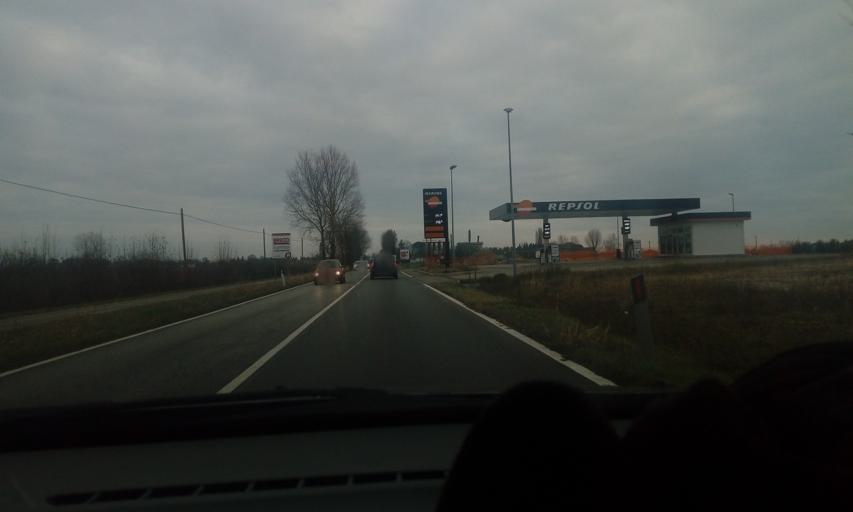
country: IT
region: Friuli Venezia Giulia
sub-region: Provincia di Udine
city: Aquileia
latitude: 45.7864
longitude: 13.3587
